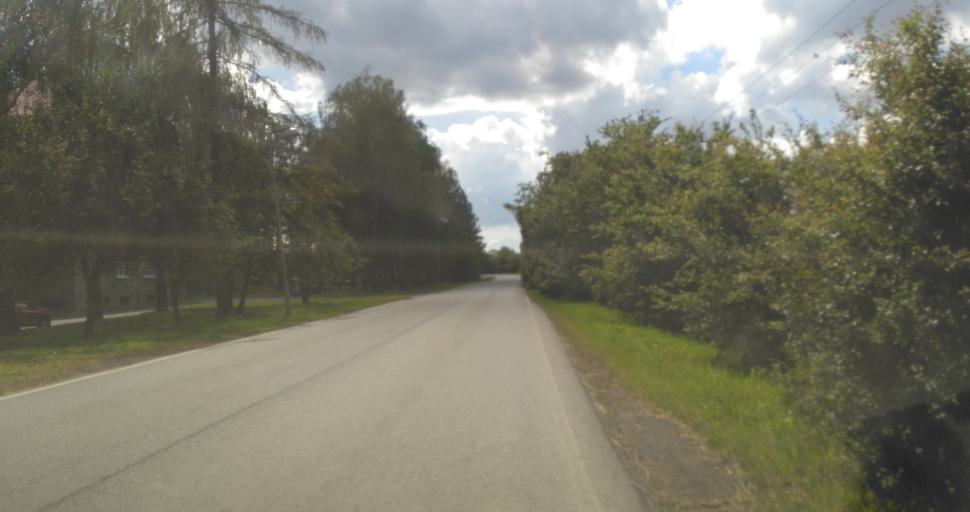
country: CZ
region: Central Bohemia
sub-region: Okres Beroun
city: Horovice
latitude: 49.8435
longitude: 13.8889
